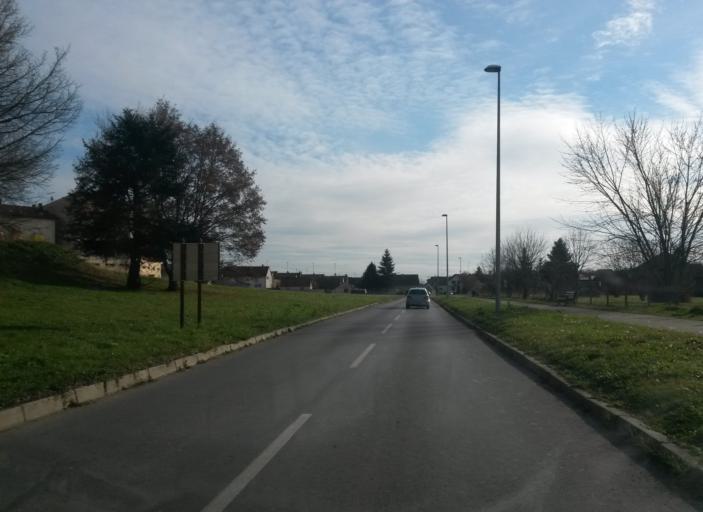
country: HR
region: Osjecko-Baranjska
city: Piskorevci
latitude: 45.3035
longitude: 18.4083
